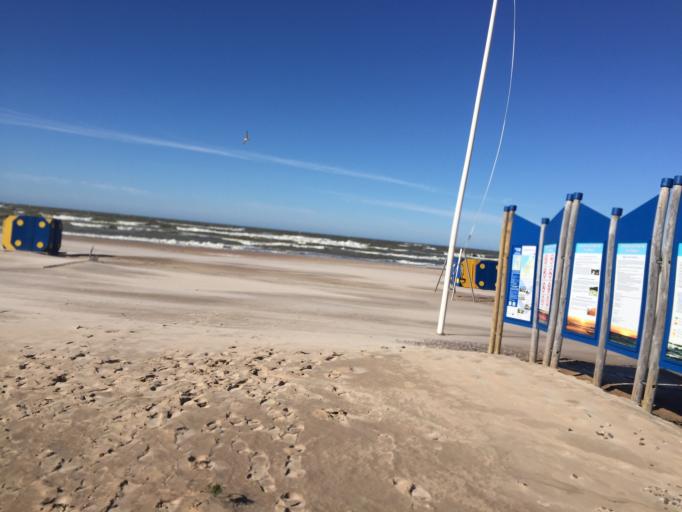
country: LV
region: Ventspils
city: Ventspils
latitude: 57.3921
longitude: 21.5301
